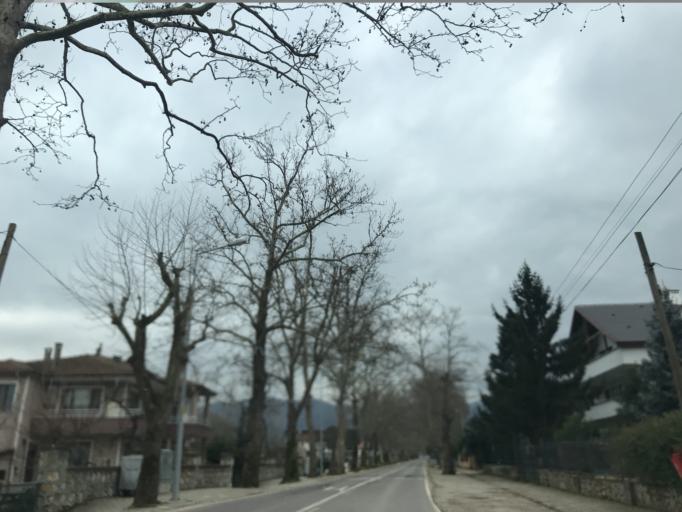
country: TR
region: Yalova
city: Kadikoy
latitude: 40.6190
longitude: 29.2183
